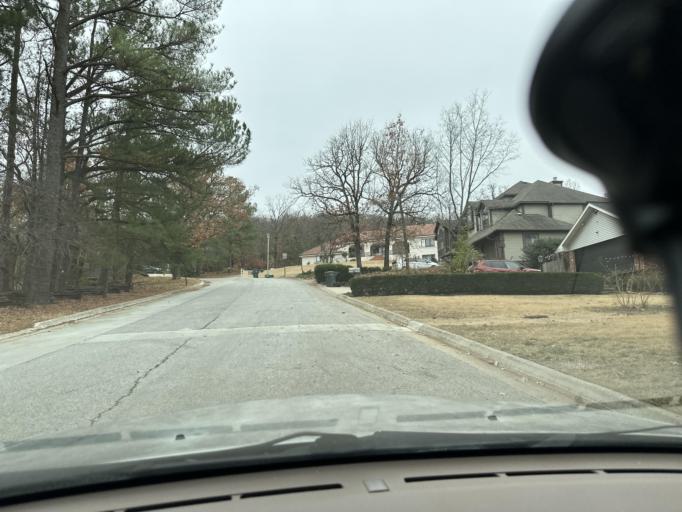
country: US
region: Arkansas
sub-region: Washington County
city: Johnson
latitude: 36.1039
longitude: -94.1447
